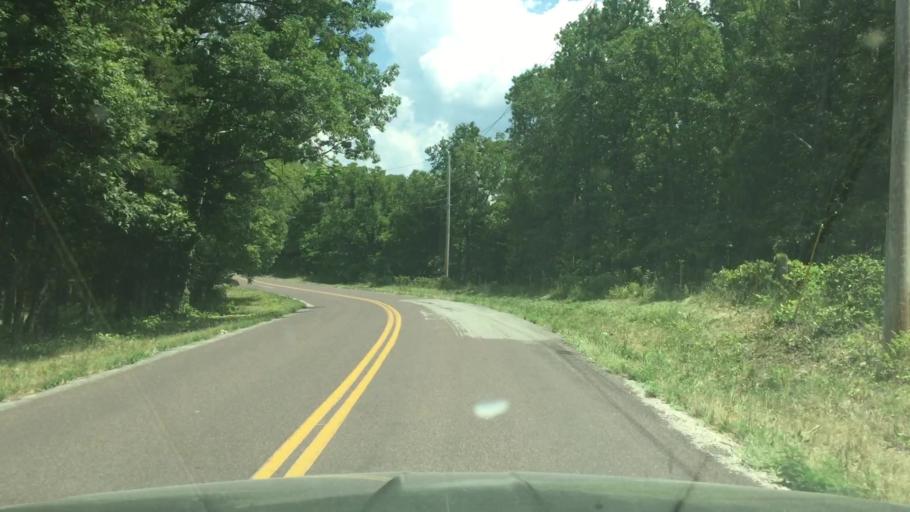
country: US
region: Missouri
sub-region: Miller County
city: Tuscumbia
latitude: 38.0918
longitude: -92.4810
